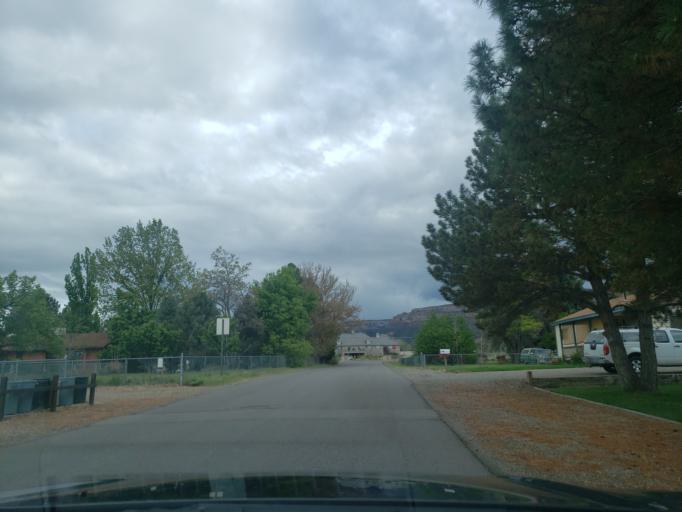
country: US
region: Colorado
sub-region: Mesa County
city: Redlands
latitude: 39.0933
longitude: -108.6626
